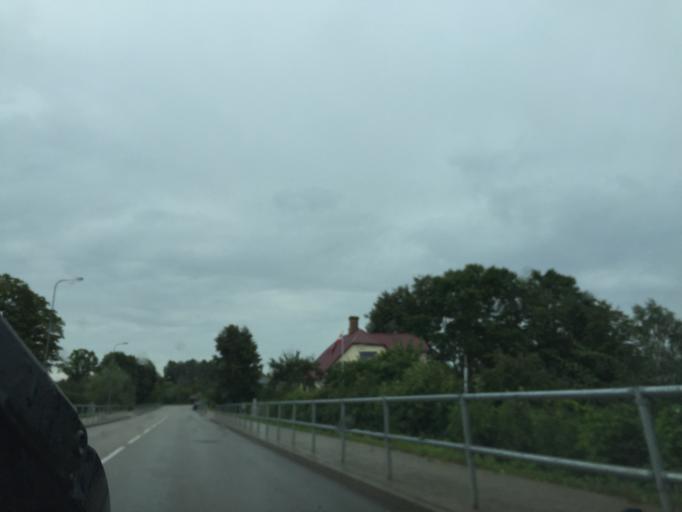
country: LV
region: Jekabpils Rajons
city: Jekabpils
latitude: 56.5009
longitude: 25.8916
